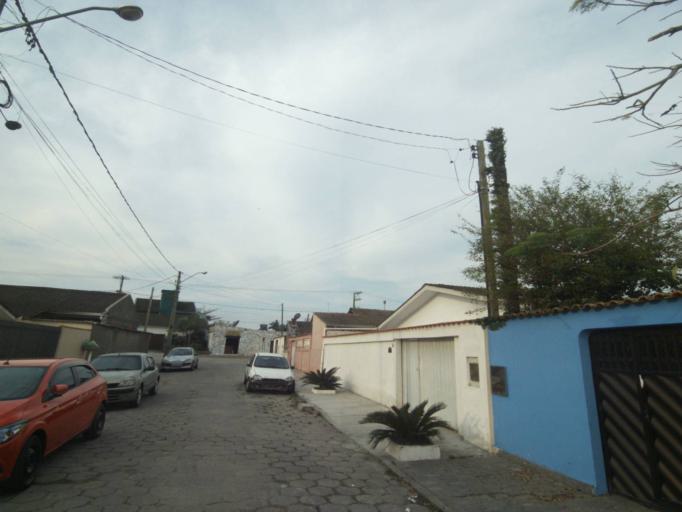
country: BR
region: Parana
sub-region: Paranagua
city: Paranagua
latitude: -25.5281
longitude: -48.5334
